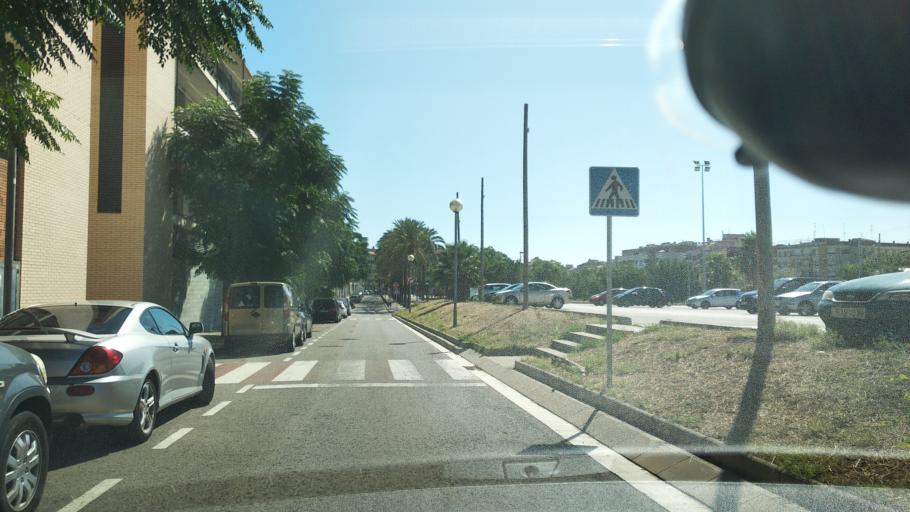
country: ES
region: Catalonia
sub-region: Provincia de Tarragona
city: El Vendrell
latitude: 41.2202
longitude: 1.5387
